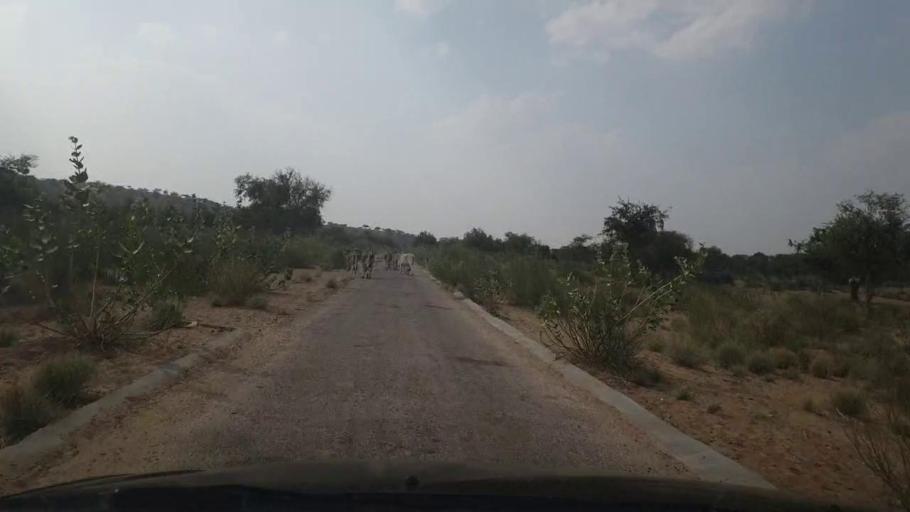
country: PK
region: Sindh
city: Islamkot
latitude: 24.9637
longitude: 70.6108
